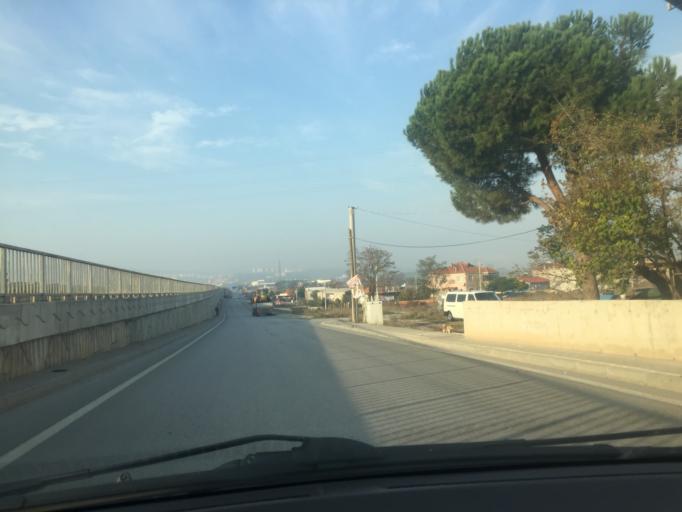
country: TR
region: Canakkale
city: Biga
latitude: 40.2420
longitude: 27.2619
